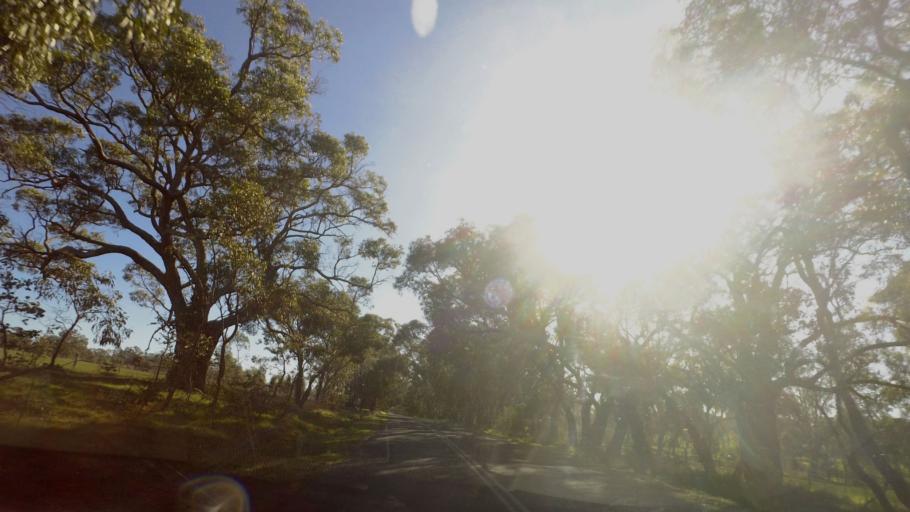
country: AU
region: Victoria
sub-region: Mount Alexander
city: Castlemaine
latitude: -36.9608
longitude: 144.3512
